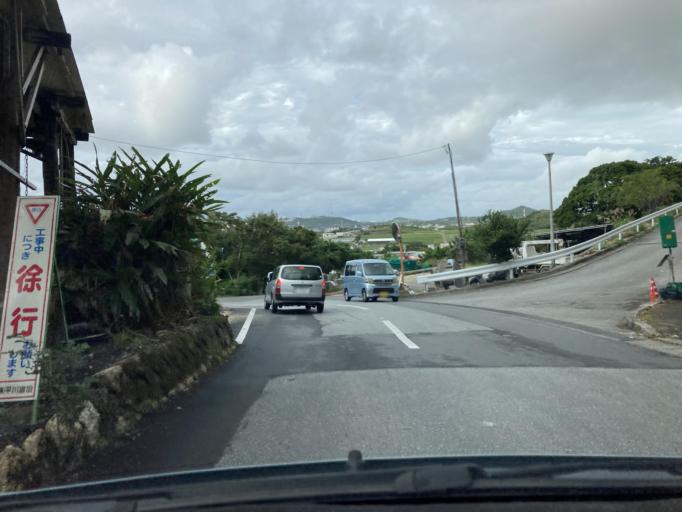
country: JP
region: Okinawa
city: Tomigusuku
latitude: 26.1788
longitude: 127.7439
